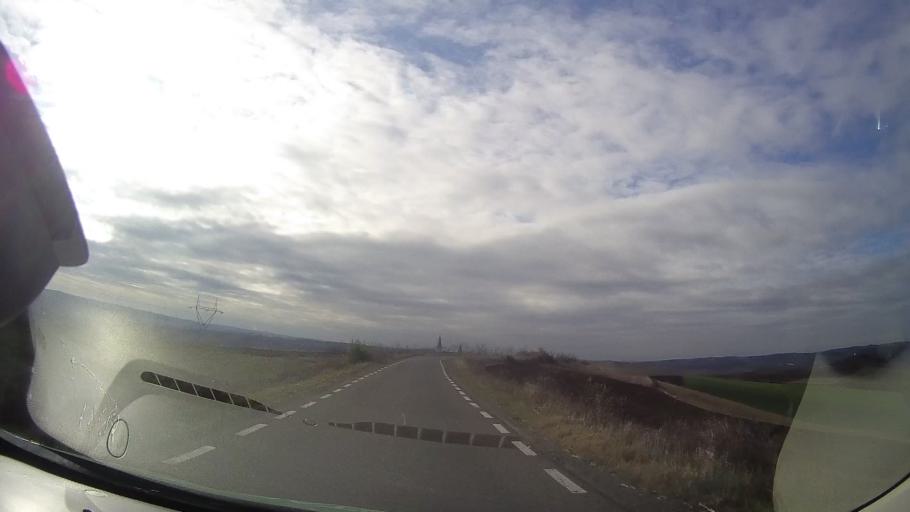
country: RO
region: Mures
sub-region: Comuna Sanger
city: Sanger
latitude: 46.5480
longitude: 24.1546
